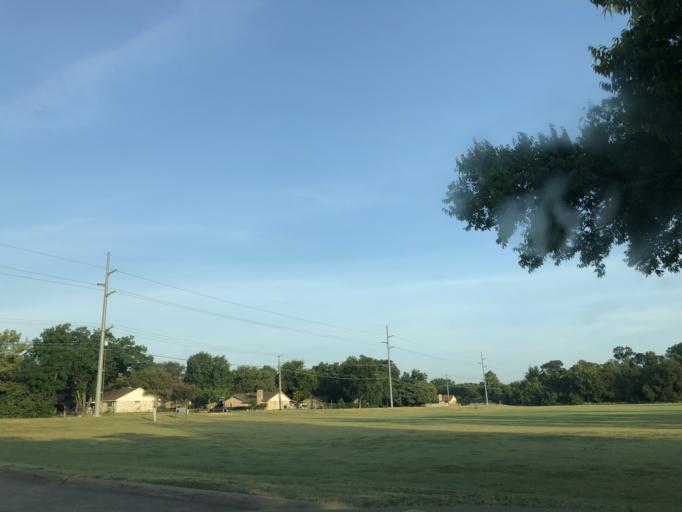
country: US
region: Texas
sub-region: Dallas County
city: Garland
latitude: 32.8632
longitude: -96.6266
